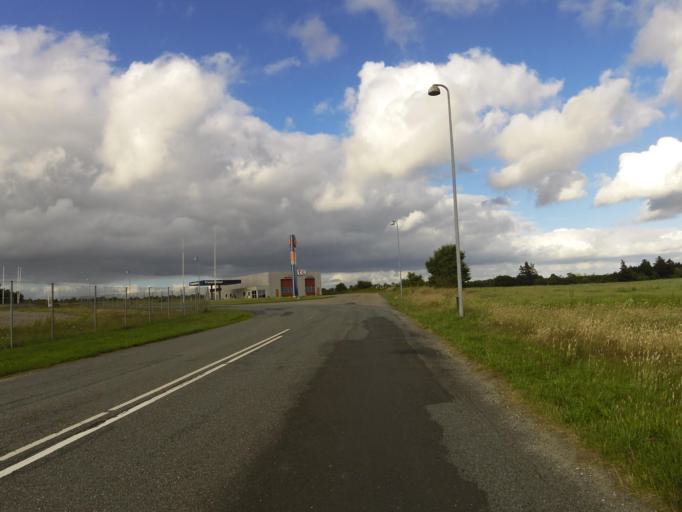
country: DK
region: South Denmark
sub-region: Tonder Kommune
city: Toftlund
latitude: 55.1746
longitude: 9.0686
